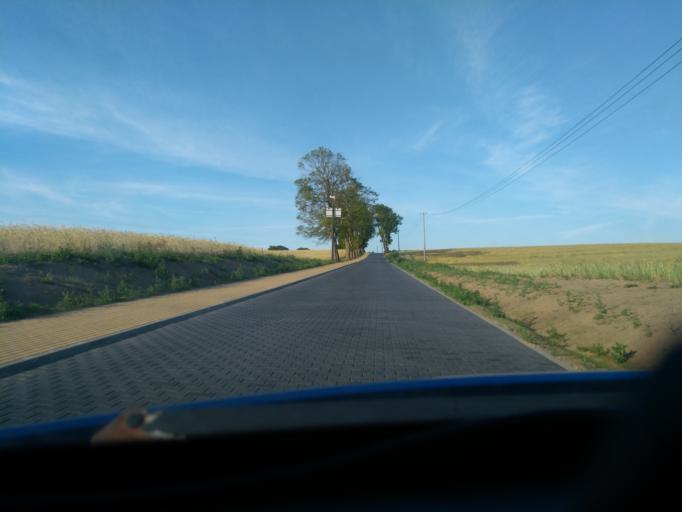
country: PL
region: Pomeranian Voivodeship
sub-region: Powiat kartuski
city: Przodkowo
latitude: 54.3938
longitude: 18.3249
